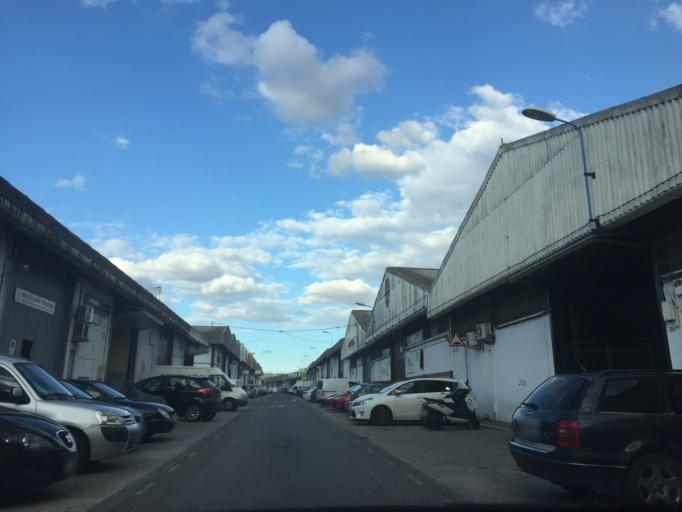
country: ES
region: Andalusia
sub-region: Provincia de Sevilla
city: Sevilla
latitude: 37.3654
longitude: -5.9593
